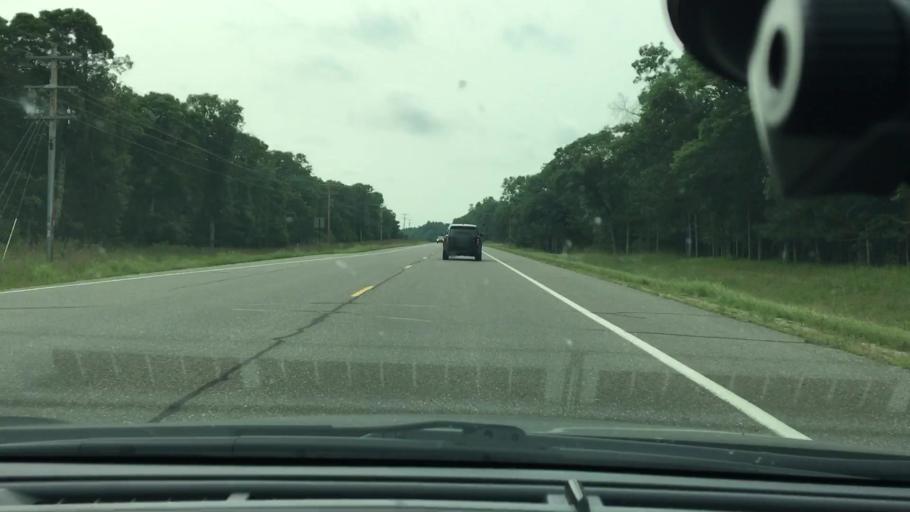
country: US
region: Minnesota
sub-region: Crow Wing County
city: Cross Lake
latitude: 46.6130
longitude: -94.1319
